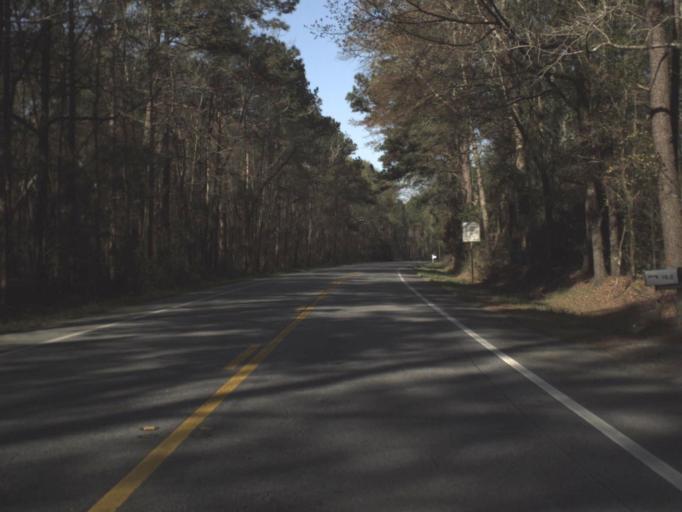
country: US
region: Georgia
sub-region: Seminole County
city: Donalsonville
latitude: 30.9765
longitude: -85.0111
